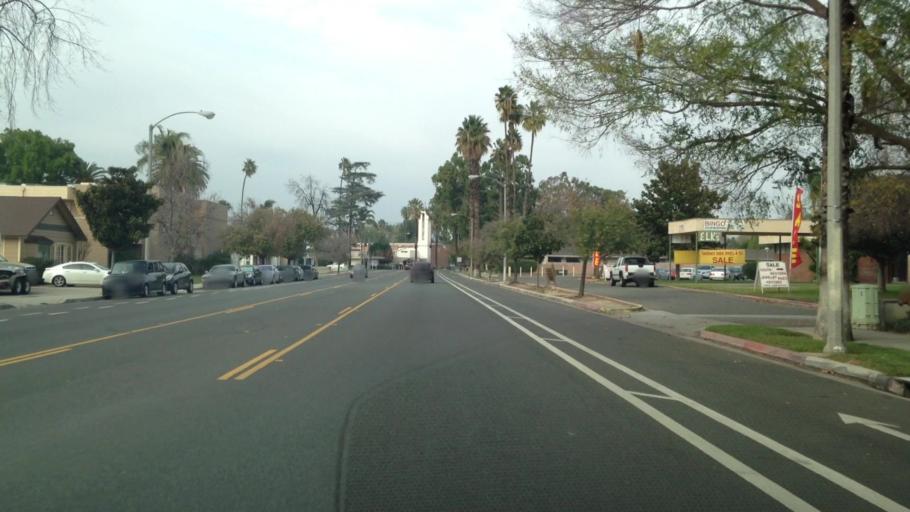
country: US
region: California
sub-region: Riverside County
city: Riverside
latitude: 33.9586
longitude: -117.3968
